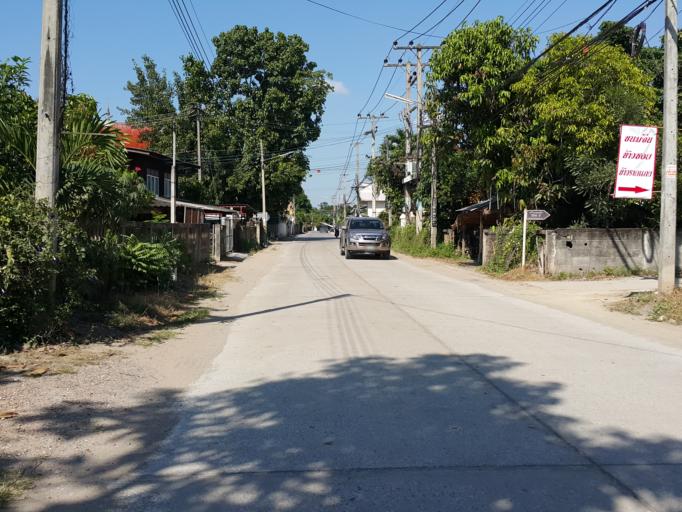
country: TH
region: Chiang Mai
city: San Kamphaeng
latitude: 18.7785
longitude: 99.1582
